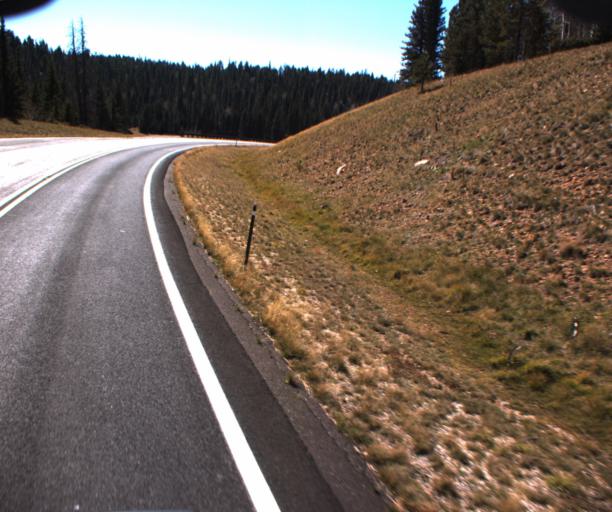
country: US
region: Arizona
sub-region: Coconino County
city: Grand Canyon
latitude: 36.4472
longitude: -112.1290
